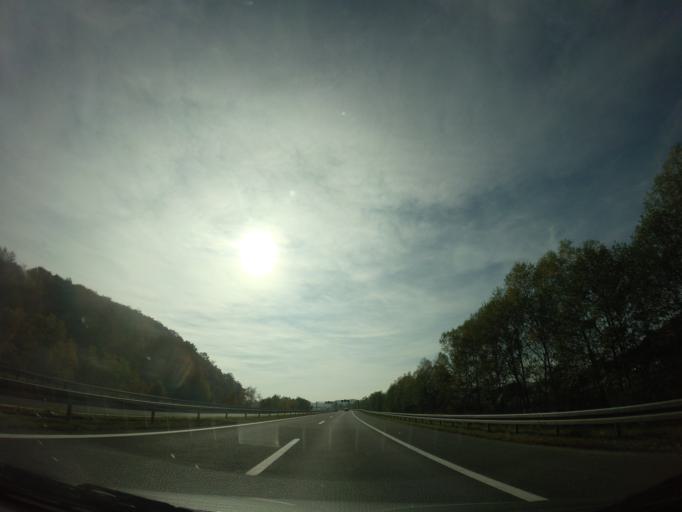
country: HR
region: Varazdinska
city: Remetinec
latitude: 46.1094
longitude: 16.2889
